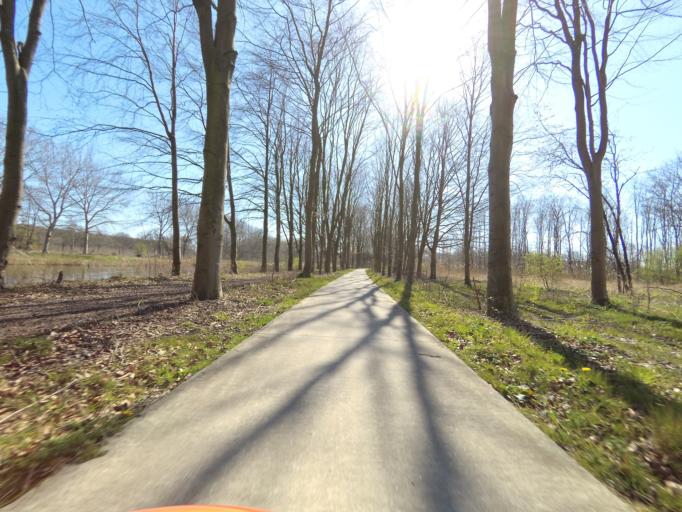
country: NL
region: Flevoland
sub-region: Gemeente Zeewolde
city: Zeewolde
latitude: 52.3384
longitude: 5.4912
